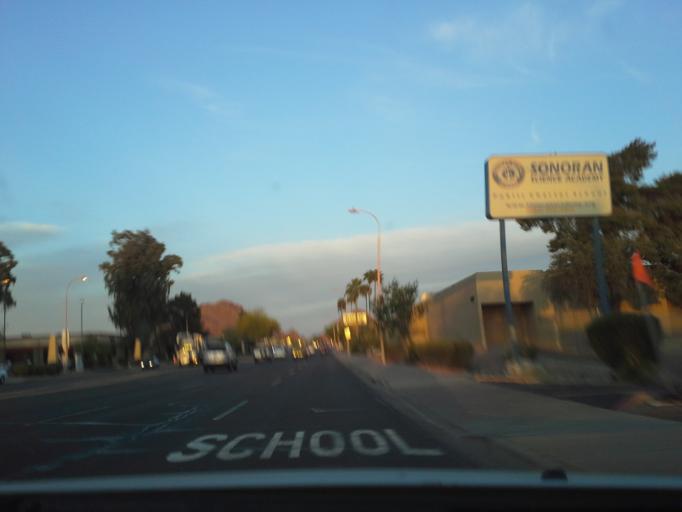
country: US
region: Arizona
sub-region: Maricopa County
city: Tempe Junction
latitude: 33.4655
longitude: -111.9779
